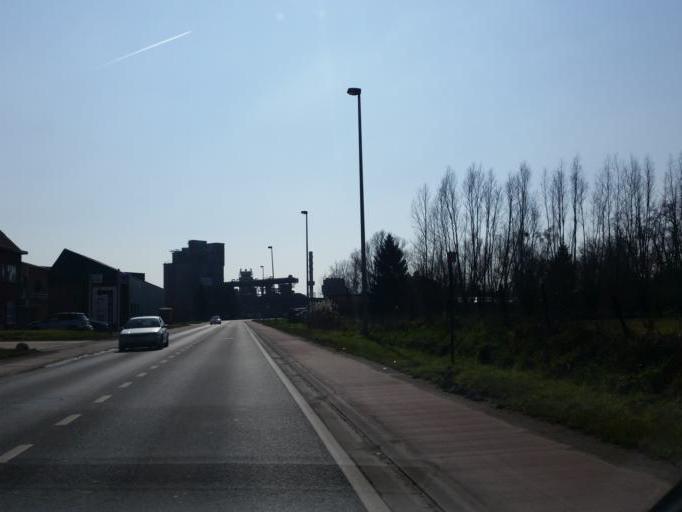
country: BE
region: Flanders
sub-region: Provincie Oost-Vlaanderen
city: Kruibeke
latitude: 51.1896
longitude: 4.3253
